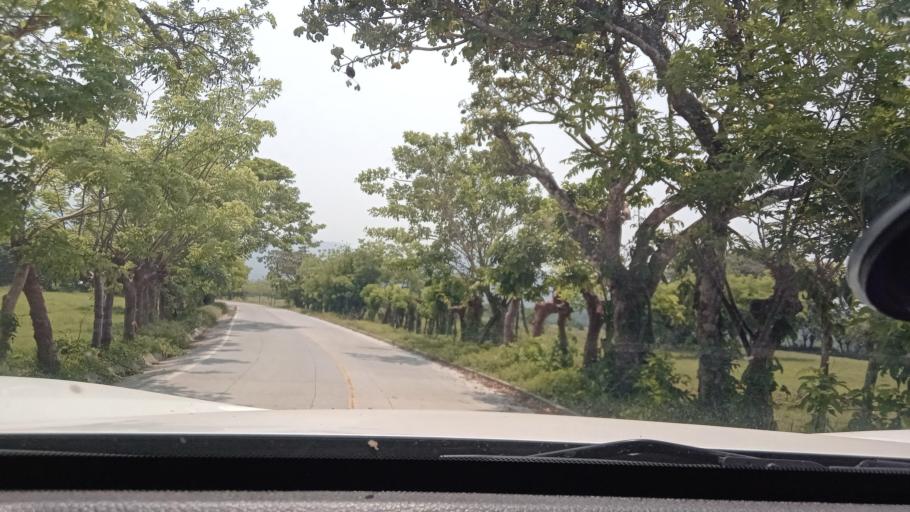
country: MX
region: Veracruz
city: Catemaco
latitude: 18.5613
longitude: -95.0358
